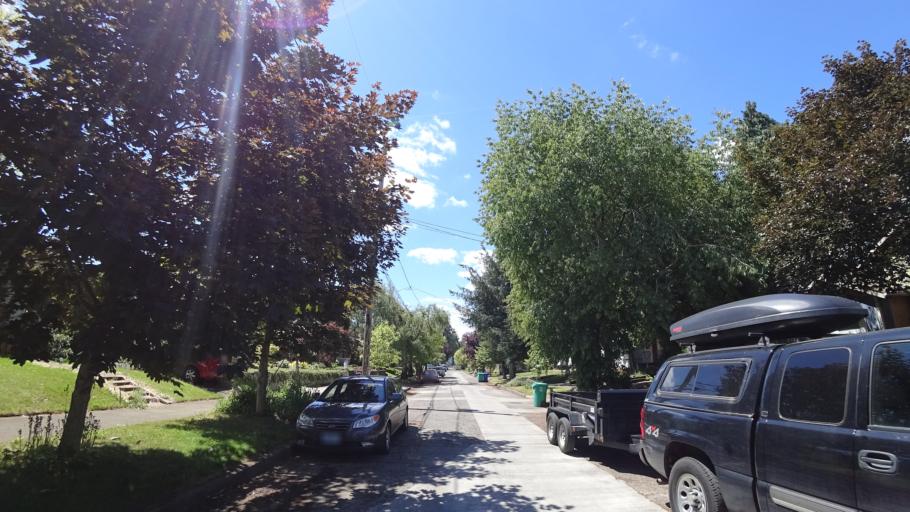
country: US
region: Oregon
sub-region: Multnomah County
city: Portland
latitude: 45.5641
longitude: -122.6831
